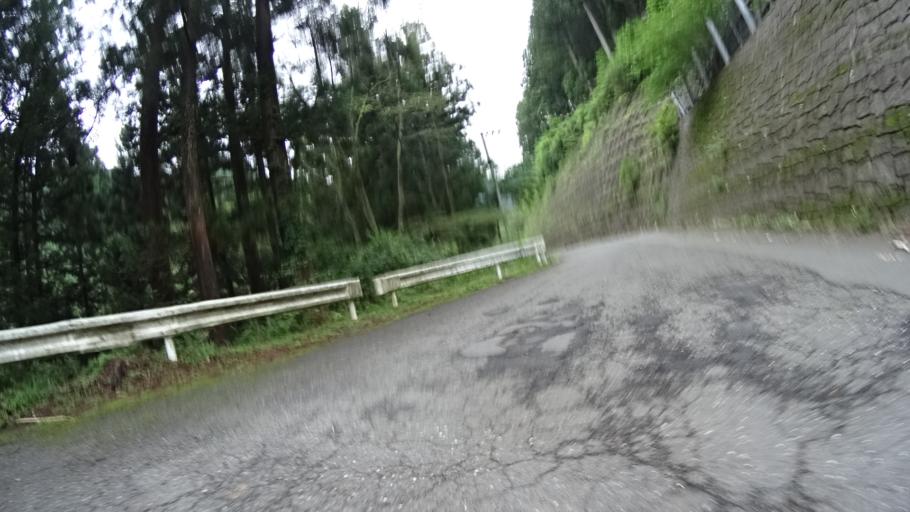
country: JP
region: Kanagawa
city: Hadano
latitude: 35.4691
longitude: 139.2174
